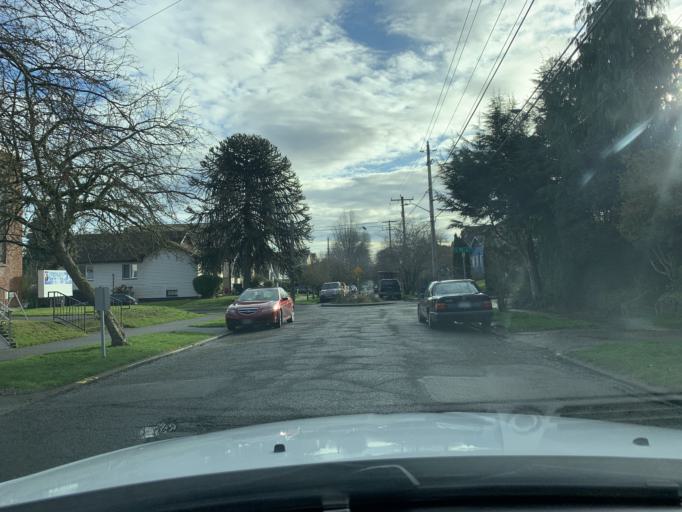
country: US
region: Washington
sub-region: King County
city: Seattle
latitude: 47.6030
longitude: -122.2989
